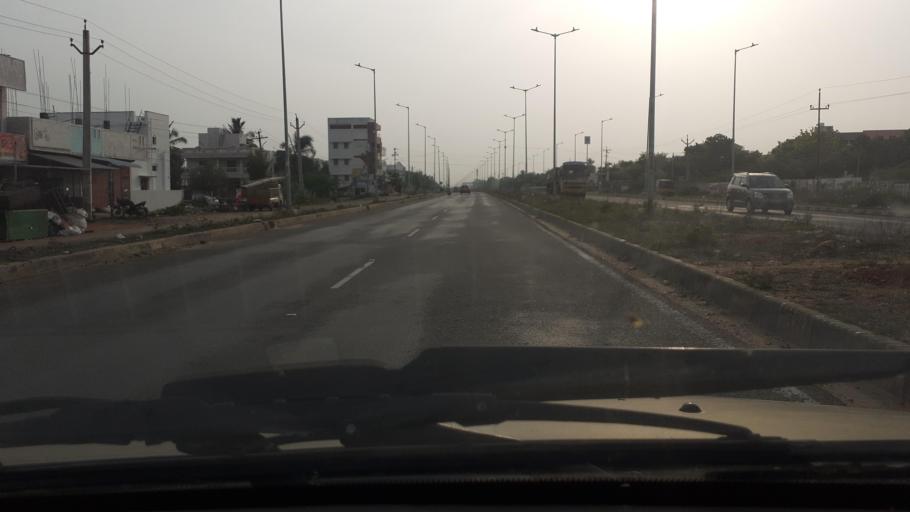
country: IN
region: Tamil Nadu
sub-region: Tirunelveli Kattabo
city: Tirunelveli
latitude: 8.7139
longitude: 77.7826
